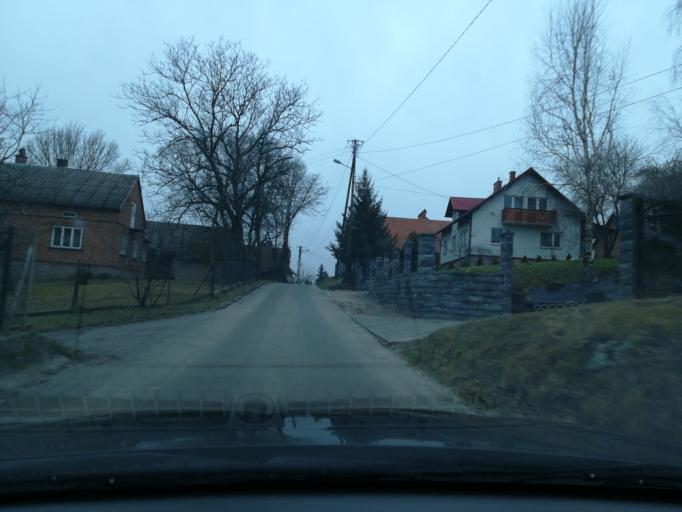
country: PL
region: Subcarpathian Voivodeship
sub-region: Powiat lancucki
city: Kosina
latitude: 50.0797
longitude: 22.3372
